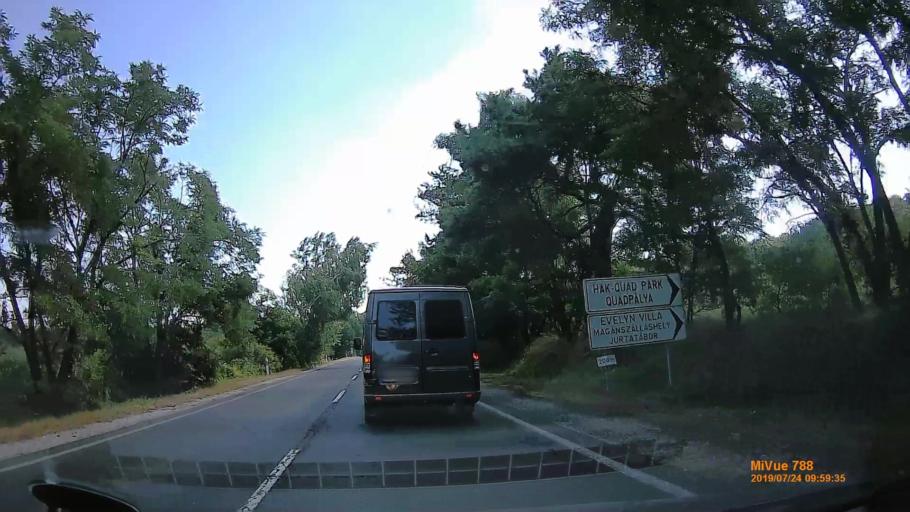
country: HU
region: Szabolcs-Szatmar-Bereg
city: Nagydobos
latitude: 48.0871
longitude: 22.2710
